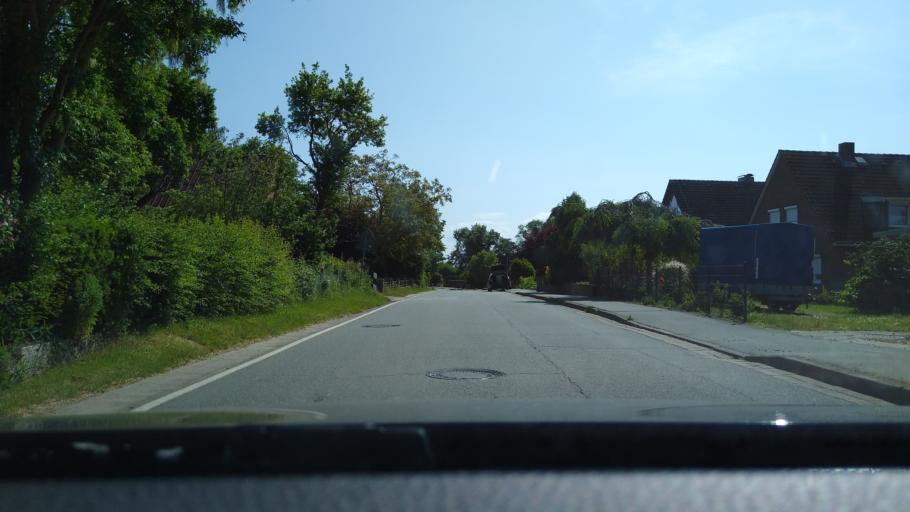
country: DE
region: Schleswig-Holstein
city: Kabelhorst
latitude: 54.2231
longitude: 10.9328
